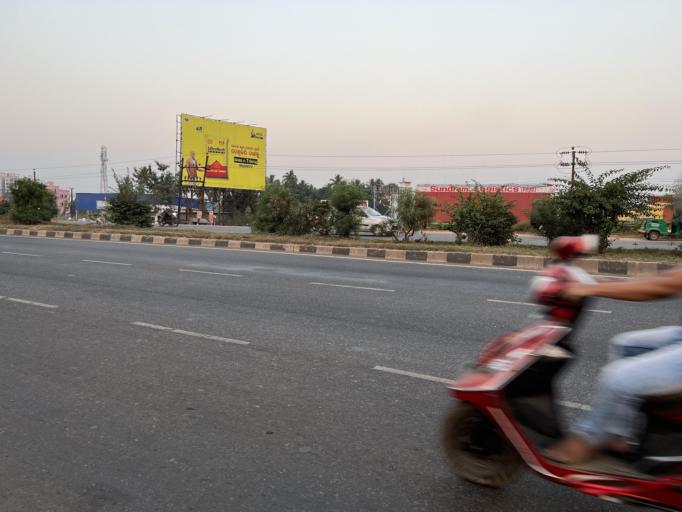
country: IN
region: Odisha
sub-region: Khordha
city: Bhubaneshwar
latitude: 20.3301
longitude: 85.8840
